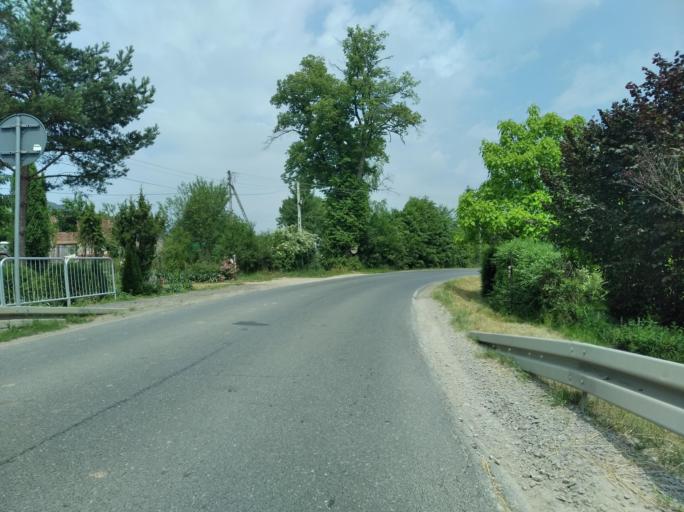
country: PL
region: Subcarpathian Voivodeship
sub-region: Powiat brzozowski
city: Humniska
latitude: 49.6728
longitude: 22.0308
